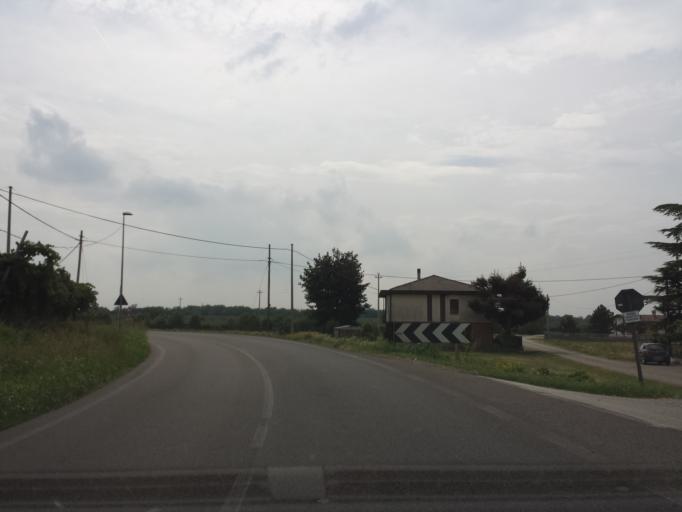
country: IT
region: Veneto
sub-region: Provincia di Vicenza
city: Gambellara
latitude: 45.4450
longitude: 11.3529
